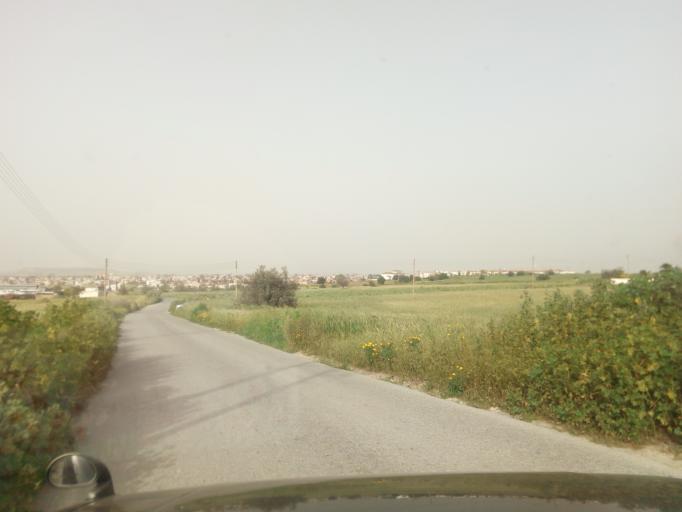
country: CY
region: Larnaka
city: Athienou
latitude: 35.0481
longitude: 33.5360
